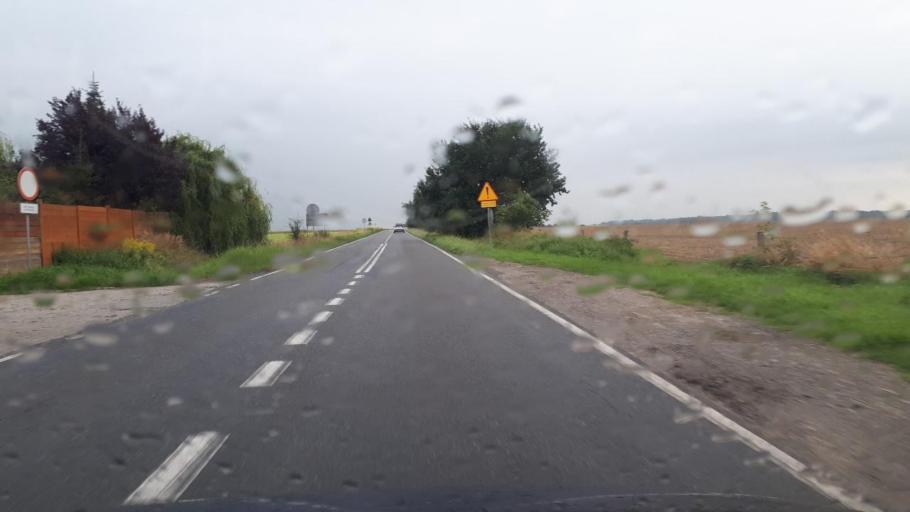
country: PL
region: Silesian Voivodeship
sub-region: Powiat tarnogorski
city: Wieszowa
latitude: 50.3670
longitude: 18.7184
